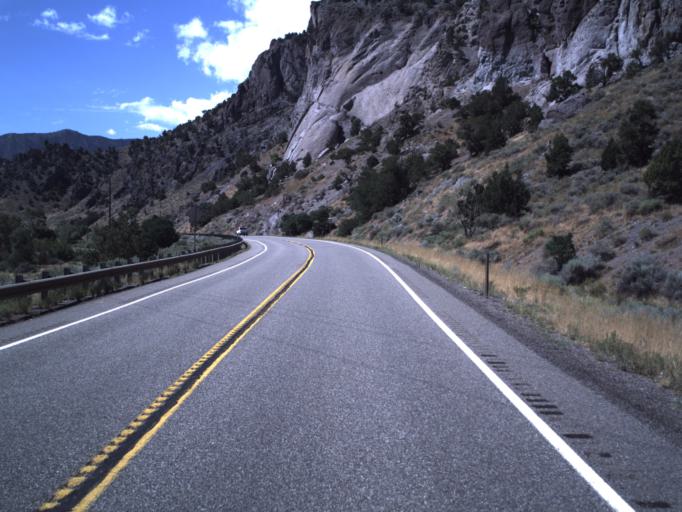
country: US
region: Utah
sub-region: Sevier County
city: Monroe
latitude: 38.5473
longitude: -112.2687
